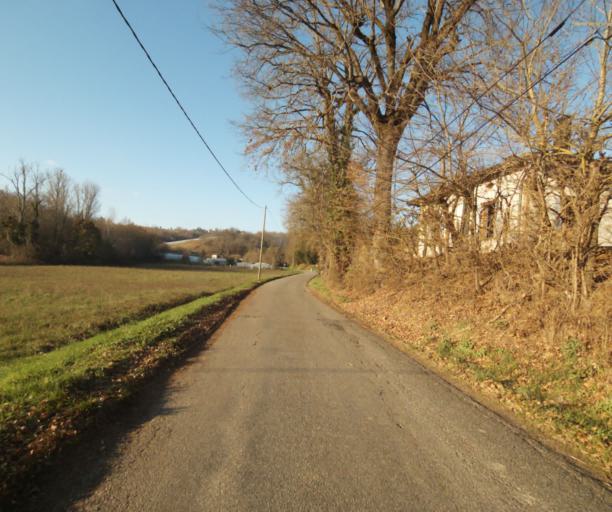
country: FR
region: Midi-Pyrenees
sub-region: Departement du Tarn-et-Garonne
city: Moissac
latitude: 44.1260
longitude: 1.1318
